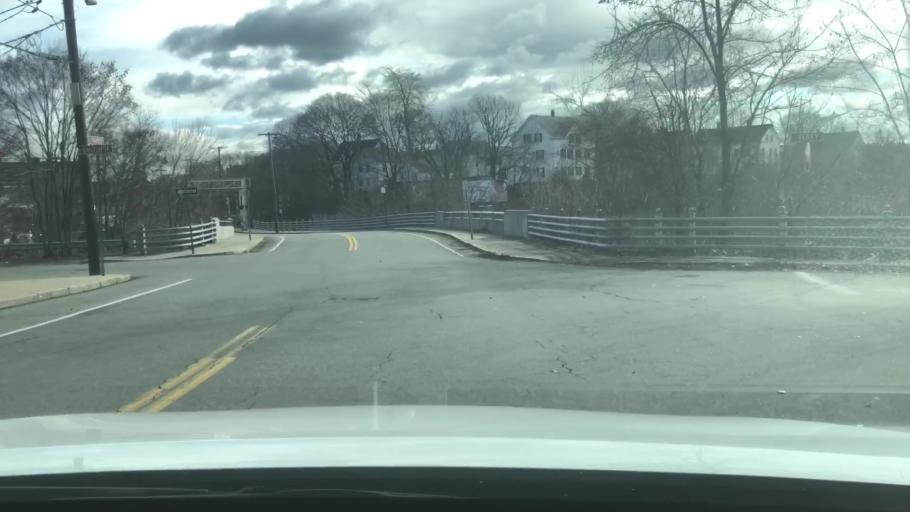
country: US
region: Rhode Island
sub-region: Providence County
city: Woonsocket
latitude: 42.0050
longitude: -71.5194
